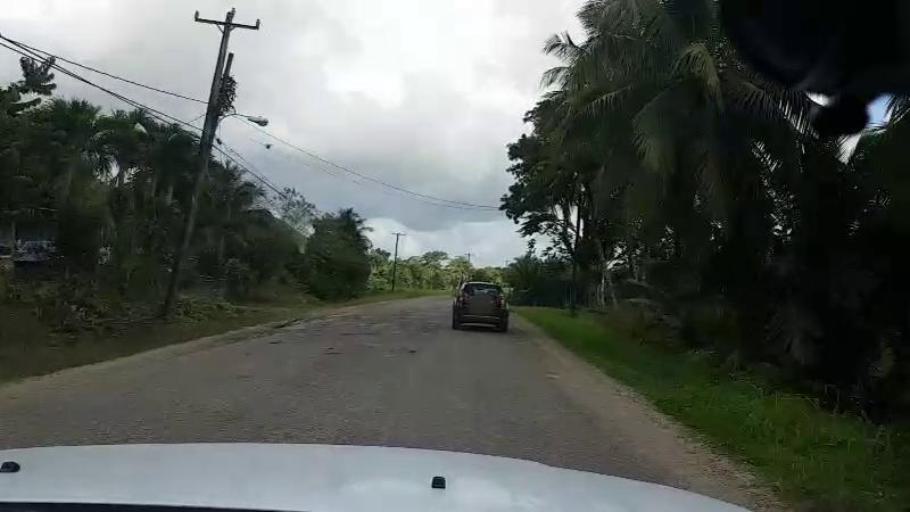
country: BZ
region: Stann Creek
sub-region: Dangriga
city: Dangriga
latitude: 17.0003
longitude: -88.4198
